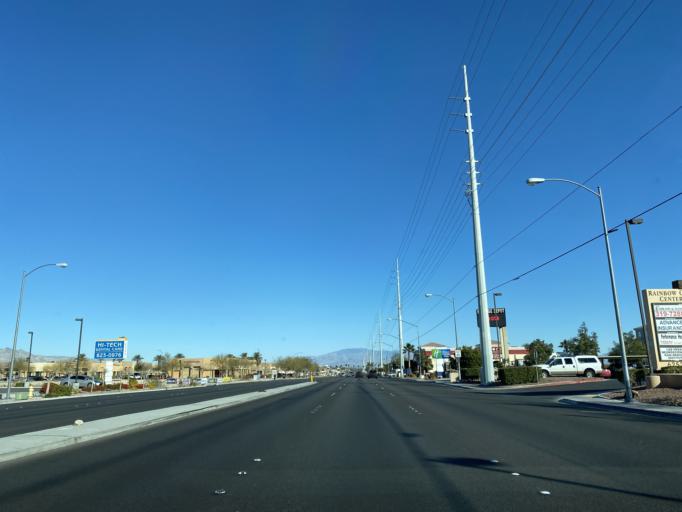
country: US
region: Nevada
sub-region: Clark County
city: Spring Valley
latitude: 36.0745
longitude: -115.2425
